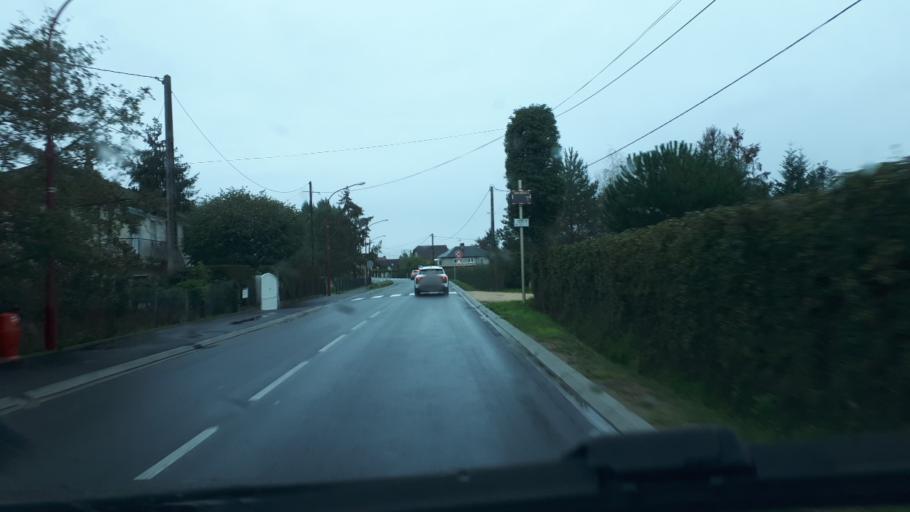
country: FR
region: Centre
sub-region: Departement du Loir-et-Cher
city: Gievres
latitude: 47.2819
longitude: 1.6672
